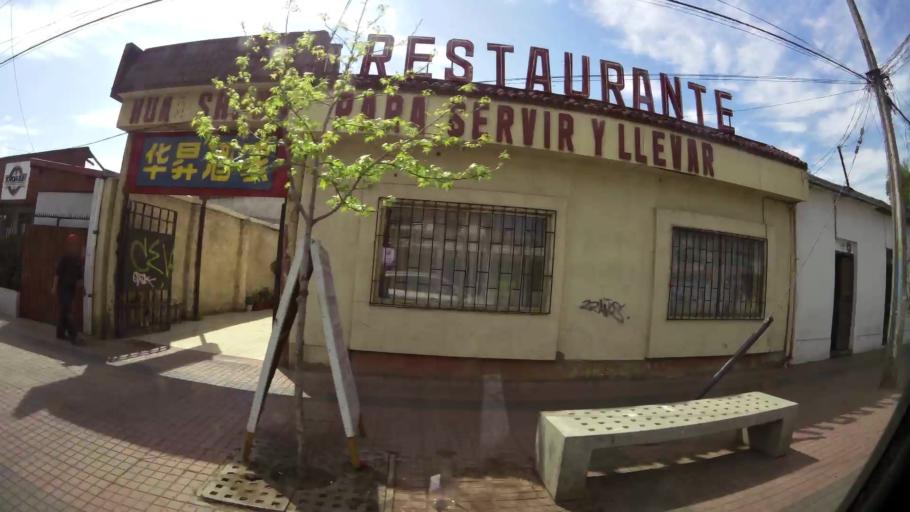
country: CL
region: Santiago Metropolitan
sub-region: Provincia de Talagante
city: Talagante
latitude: -33.6629
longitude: -70.9246
